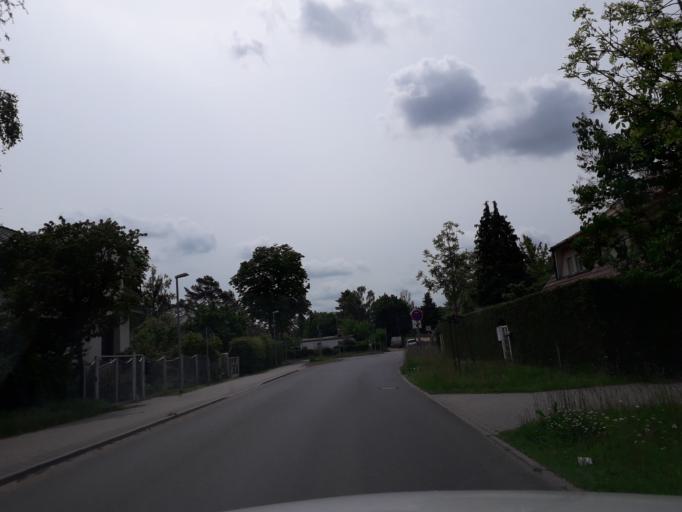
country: DE
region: Brandenburg
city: Brieselang
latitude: 52.6054
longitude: 12.9898
